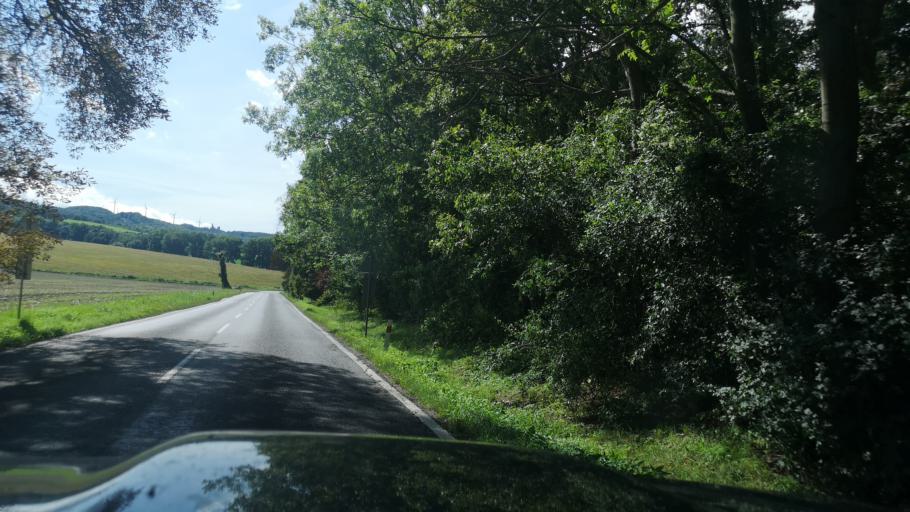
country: SK
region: Trnavsky
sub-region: Okres Senica
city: Senica
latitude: 48.5949
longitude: 17.4022
